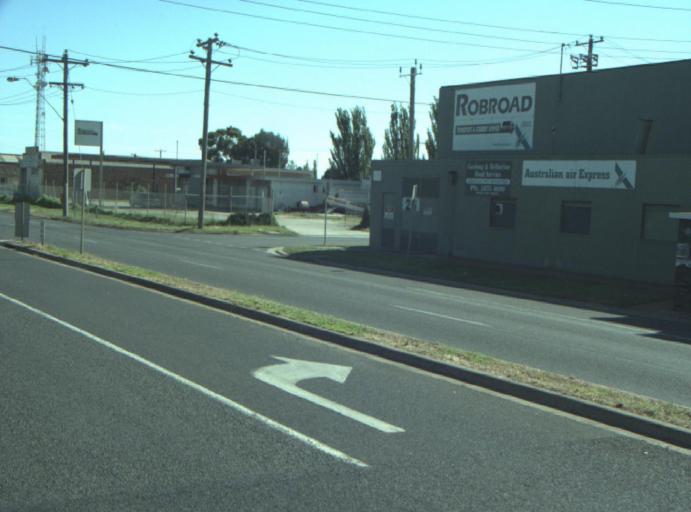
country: AU
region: Victoria
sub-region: Greater Geelong
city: Bell Park
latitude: -38.0930
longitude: 144.3658
